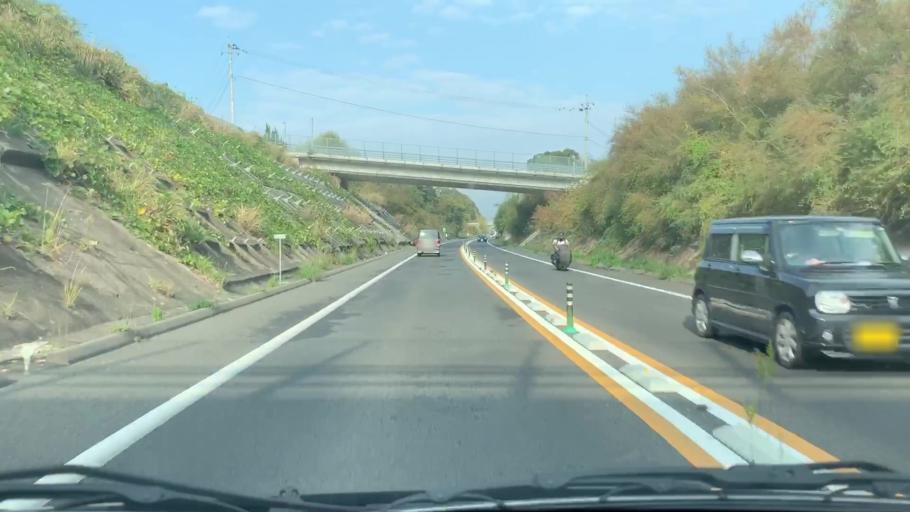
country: JP
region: Nagasaki
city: Sasebo
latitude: 33.0201
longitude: 129.7328
